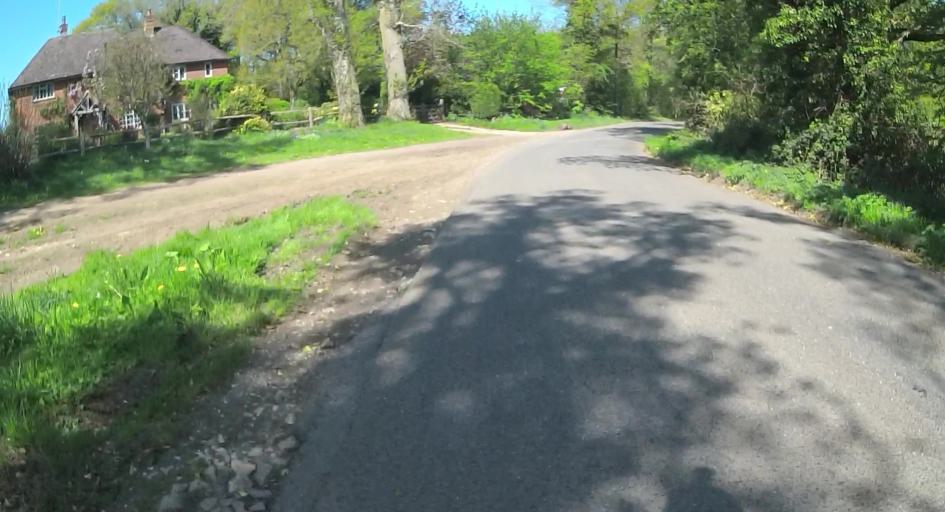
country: GB
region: England
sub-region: Hampshire
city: Alton
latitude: 51.1641
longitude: -1.0236
